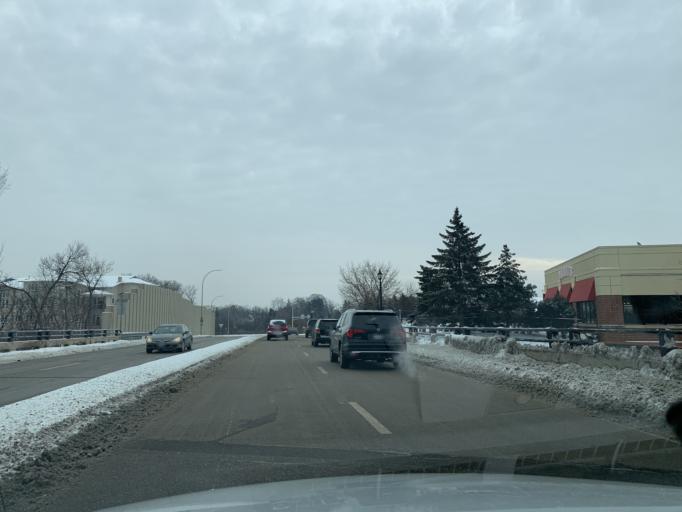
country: US
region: Minnesota
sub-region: Hennepin County
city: Edina
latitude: 44.9122
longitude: -93.3539
